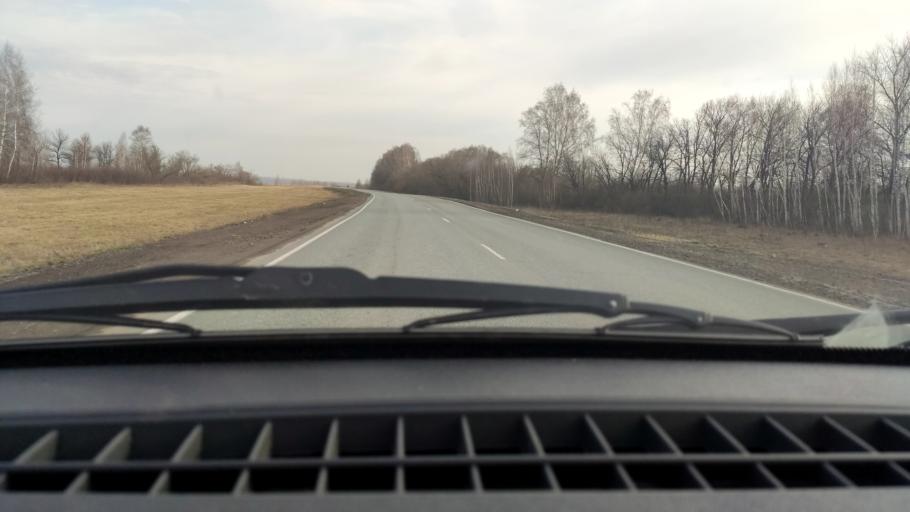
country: RU
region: Bashkortostan
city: Chishmy
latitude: 54.4096
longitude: 55.2211
